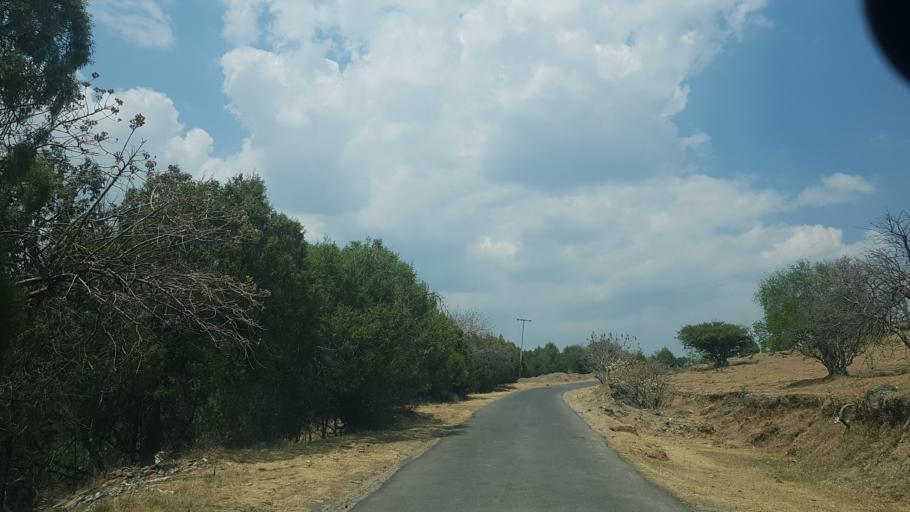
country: MX
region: Puebla
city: San Juan Amecac
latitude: 18.8150
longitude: -98.6246
